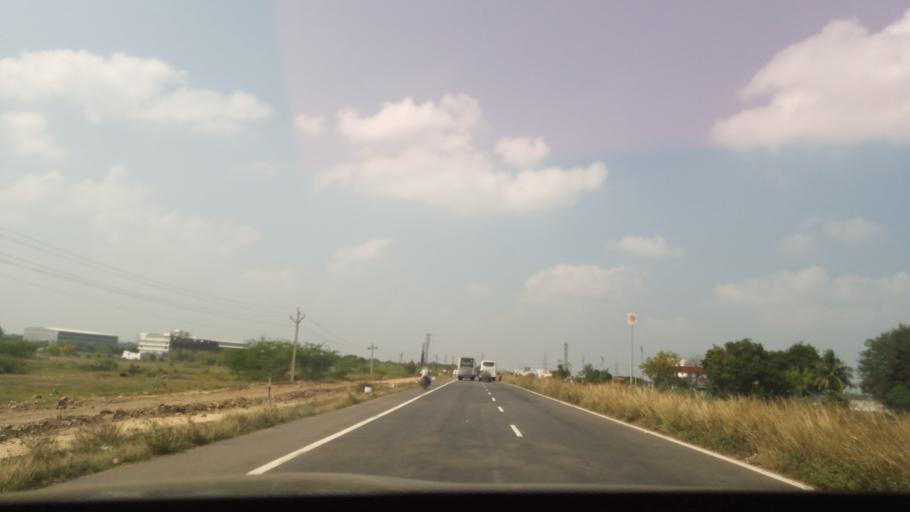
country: IN
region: Tamil Nadu
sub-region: Kancheepuram
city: Kanchipuram
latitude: 12.8735
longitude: 79.7450
